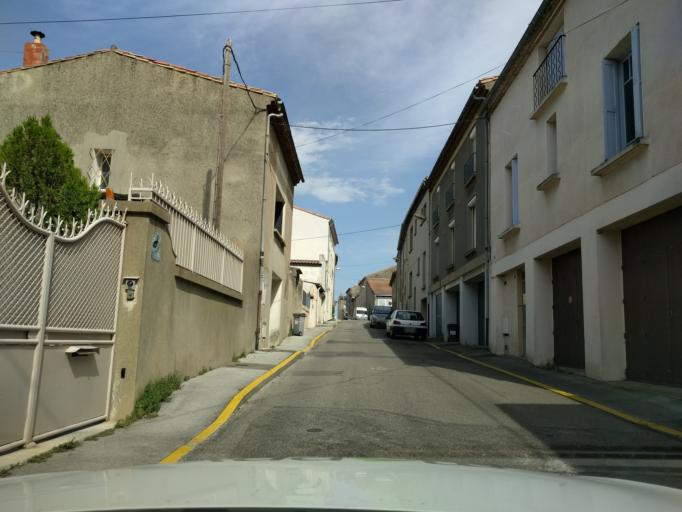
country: FR
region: Languedoc-Roussillon
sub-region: Departement de l'Aude
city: Carcassonne
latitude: 43.2129
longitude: 2.3428
